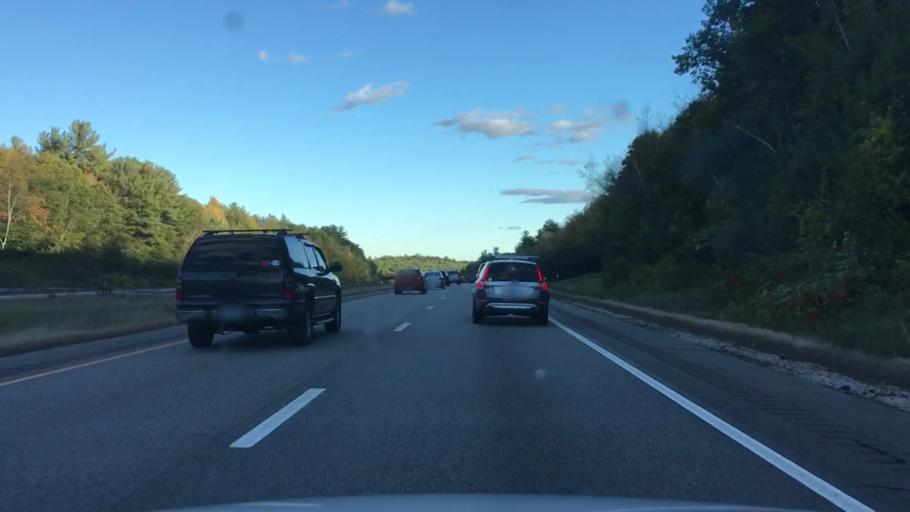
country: US
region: New Hampshire
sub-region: Rockingham County
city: Raymond
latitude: 43.0252
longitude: -71.2371
